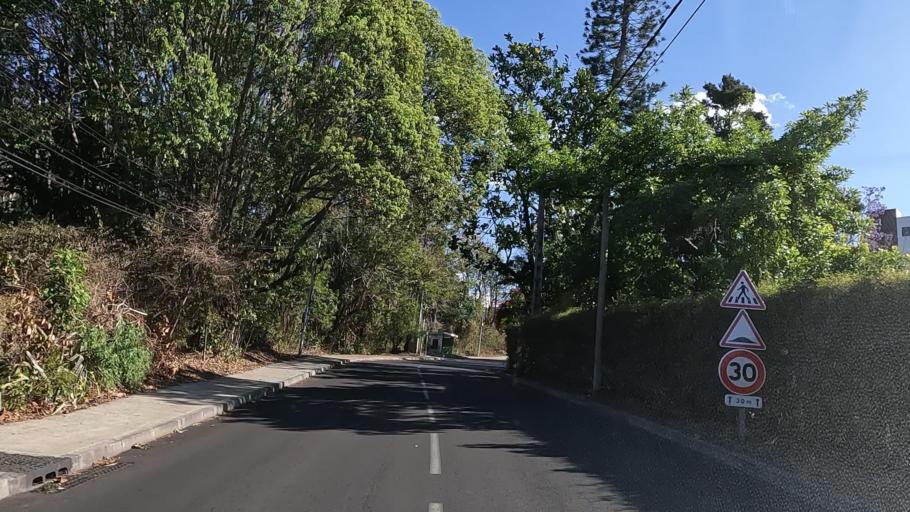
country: RE
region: Reunion
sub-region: Reunion
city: Le Tampon
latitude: -21.2603
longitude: 55.5095
